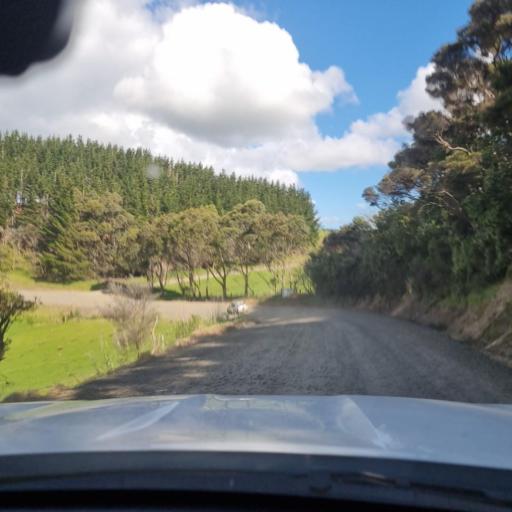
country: NZ
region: Auckland
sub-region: Auckland
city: Wellsford
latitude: -36.3347
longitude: 174.1556
